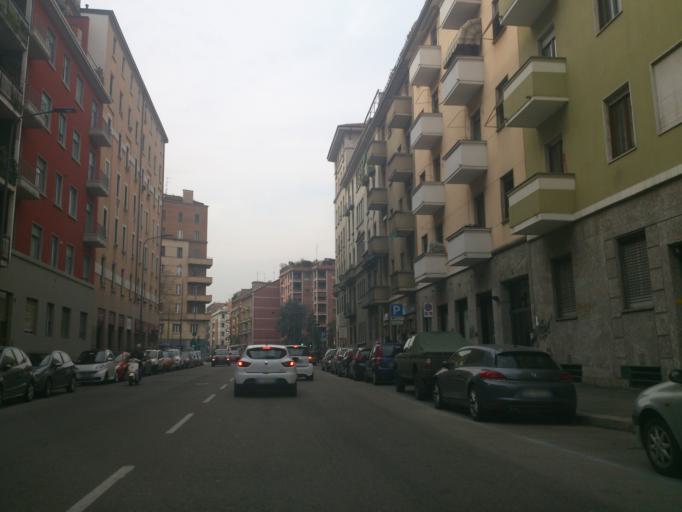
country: IT
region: Lombardy
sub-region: Citta metropolitana di Milano
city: Milano
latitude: 45.4550
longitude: 9.2176
